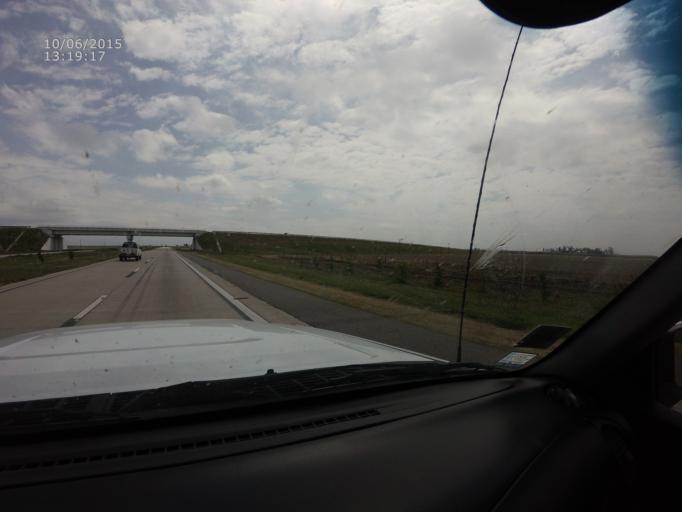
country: AR
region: Cordoba
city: Marcos Juarez
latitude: -32.6778
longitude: -62.0290
